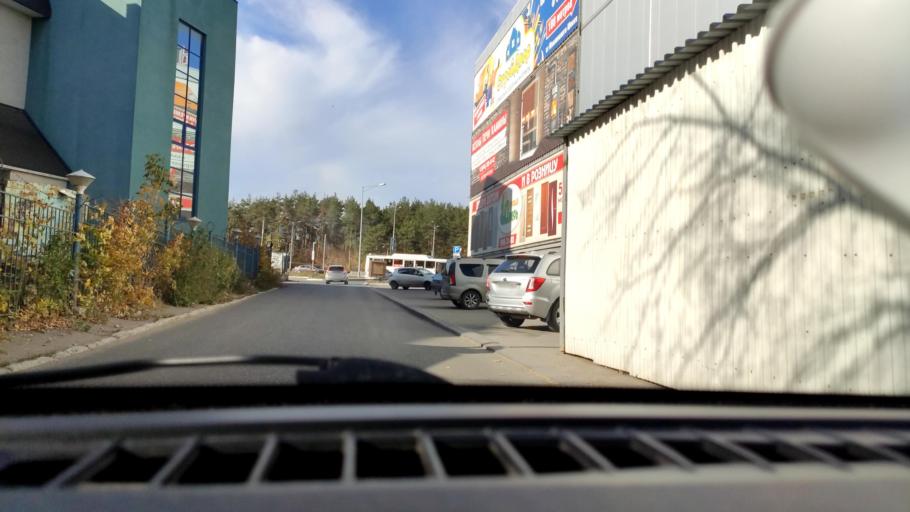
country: RU
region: Samara
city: Samara
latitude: 53.2630
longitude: 50.2454
